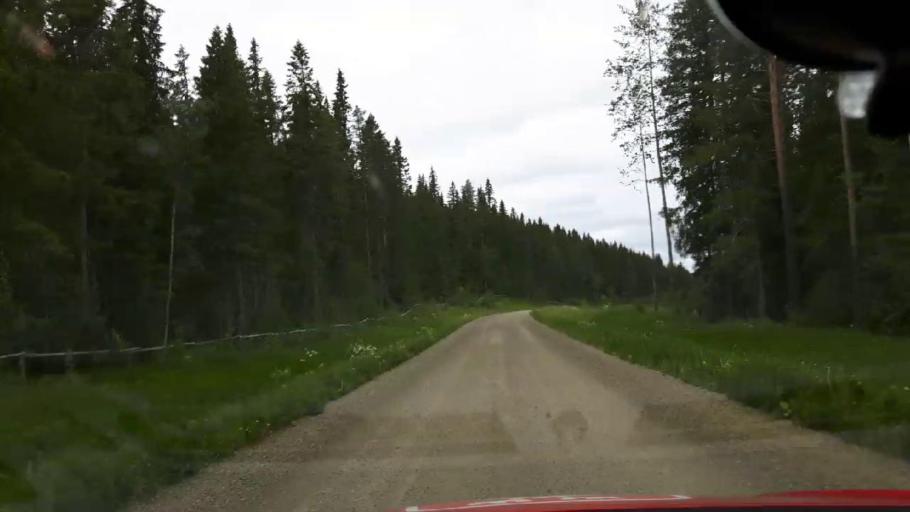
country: SE
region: Jaemtland
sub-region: OEstersunds Kommun
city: Brunflo
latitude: 62.9265
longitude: 15.0041
